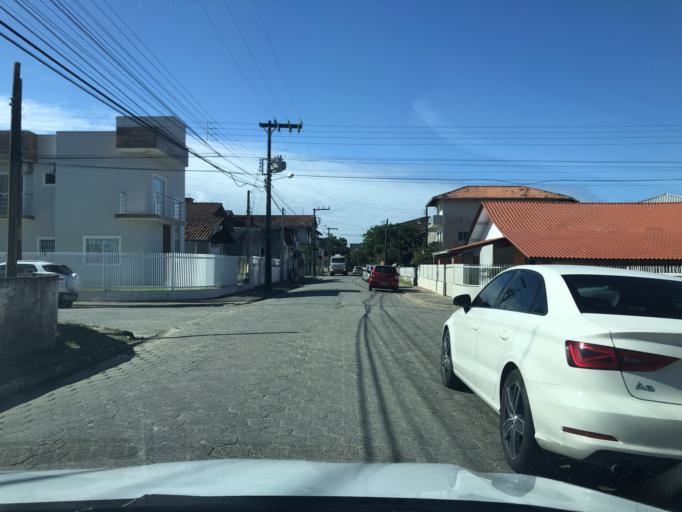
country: BR
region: Santa Catarina
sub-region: Sao Francisco Do Sul
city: Sao Francisco do Sul
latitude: -26.2247
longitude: -48.5196
